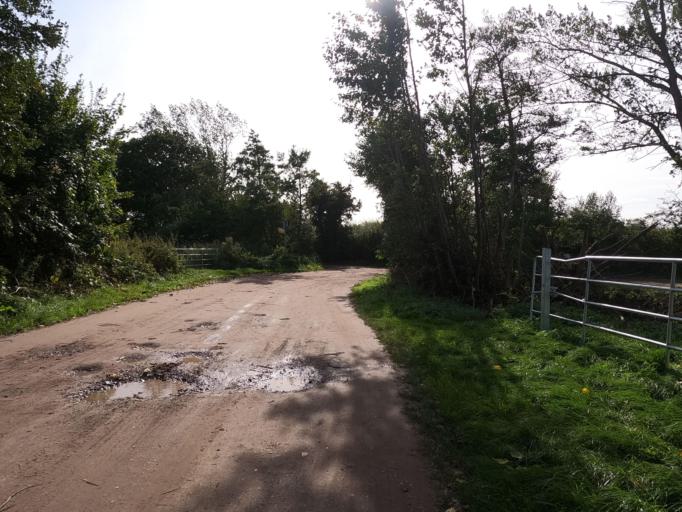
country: DE
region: Schleswig-Holstein
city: Dahme
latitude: 54.1990
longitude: 11.0894
